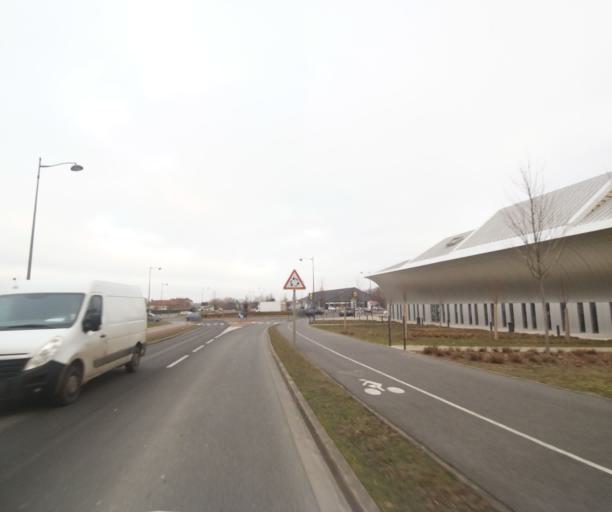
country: FR
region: Champagne-Ardenne
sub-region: Departement de la Haute-Marne
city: Bettancourt-la-Ferree
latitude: 48.6471
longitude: 4.9578
